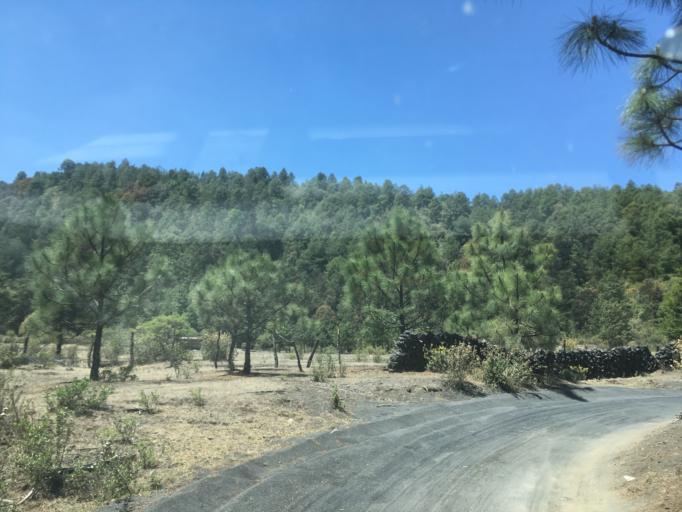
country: MX
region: Michoacan
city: Angahuan
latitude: 19.4793
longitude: -102.2485
